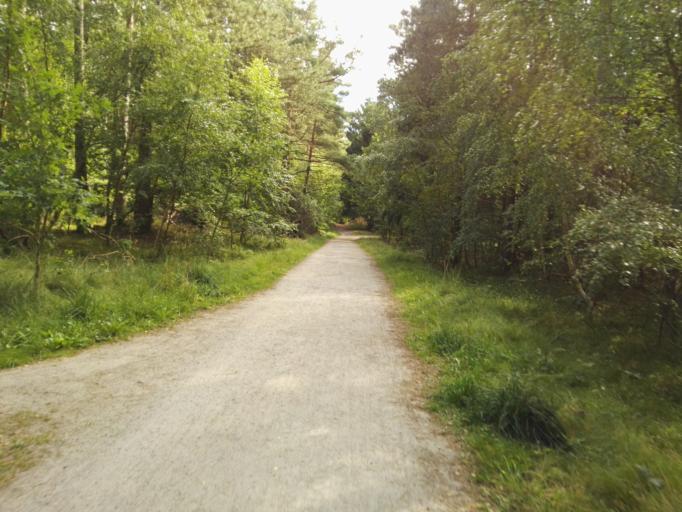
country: DK
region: Zealand
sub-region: Odsherred Kommune
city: Nykobing Sjaelland
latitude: 55.9455
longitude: 11.7031
